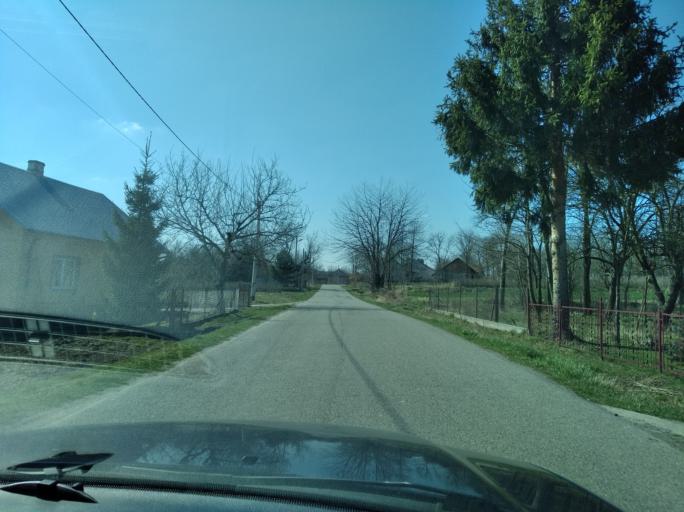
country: PL
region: Subcarpathian Voivodeship
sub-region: Powiat jaroslawski
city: Jodlowka
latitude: 49.9277
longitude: 22.4793
